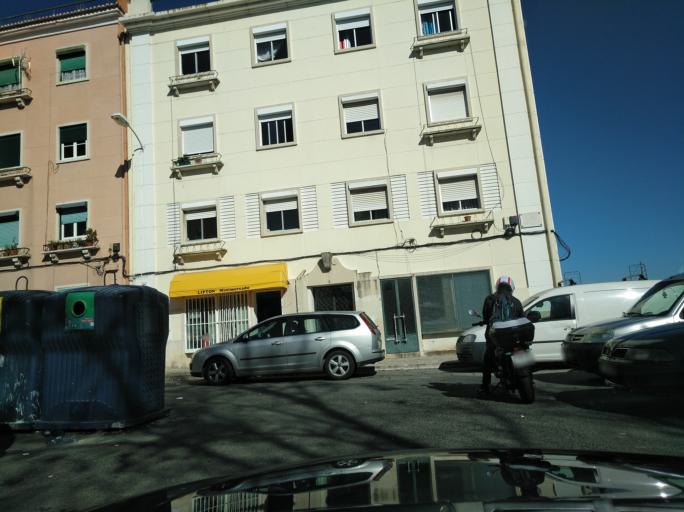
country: PT
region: Lisbon
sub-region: Lisbon
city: Lisbon
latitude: 38.7265
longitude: -9.1170
